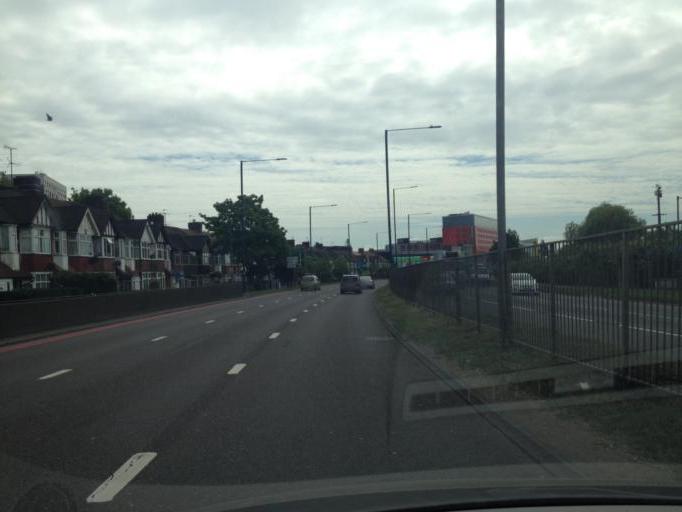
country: GB
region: England
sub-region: Greater London
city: Acton
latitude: 51.5237
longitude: -0.2659
